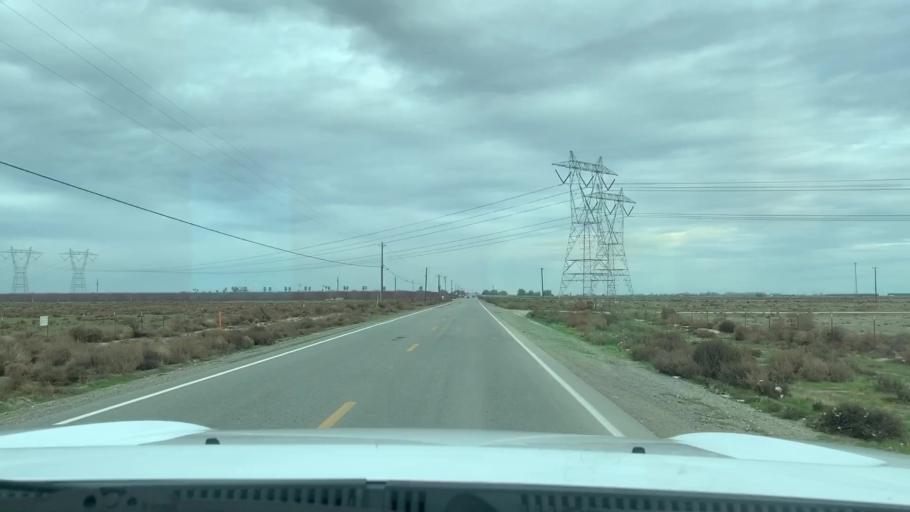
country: US
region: California
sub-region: Kern County
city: Rosedale
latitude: 35.2781
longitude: -119.2526
